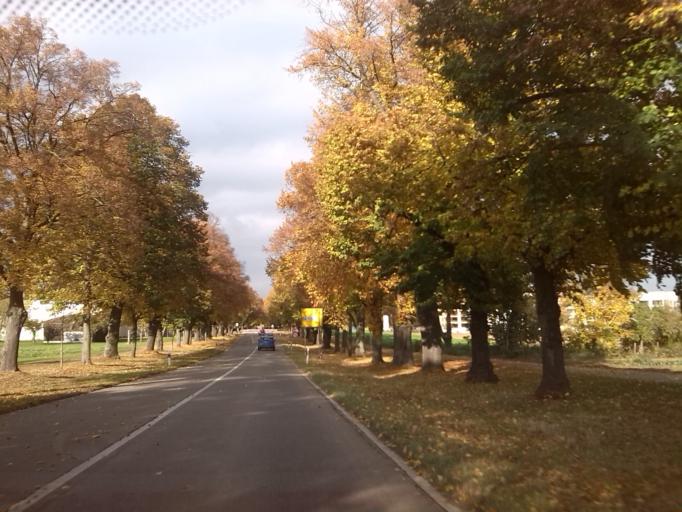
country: DE
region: Baden-Wuerttemberg
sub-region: Regierungsbezirk Stuttgart
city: Kornwestheim
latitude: 48.8765
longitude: 9.1861
